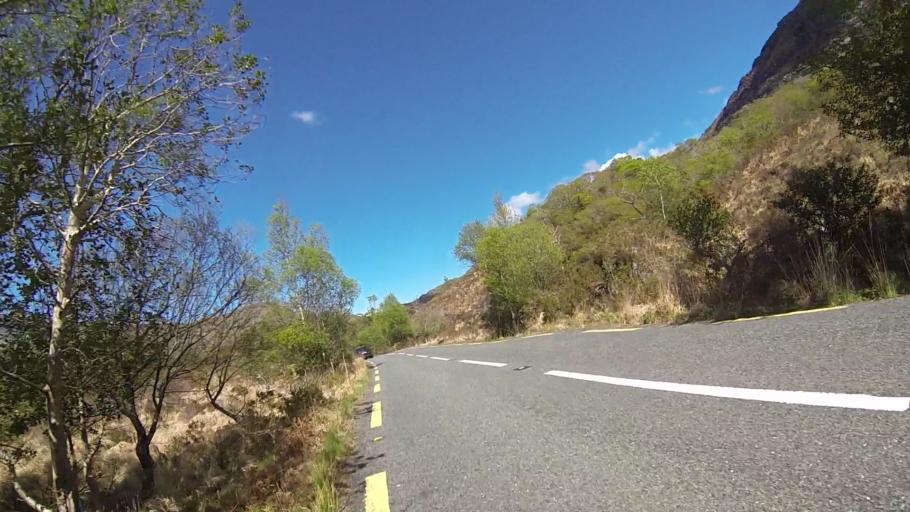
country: IE
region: Munster
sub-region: Ciarrai
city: Kenmare
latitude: 51.9758
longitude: -9.5769
